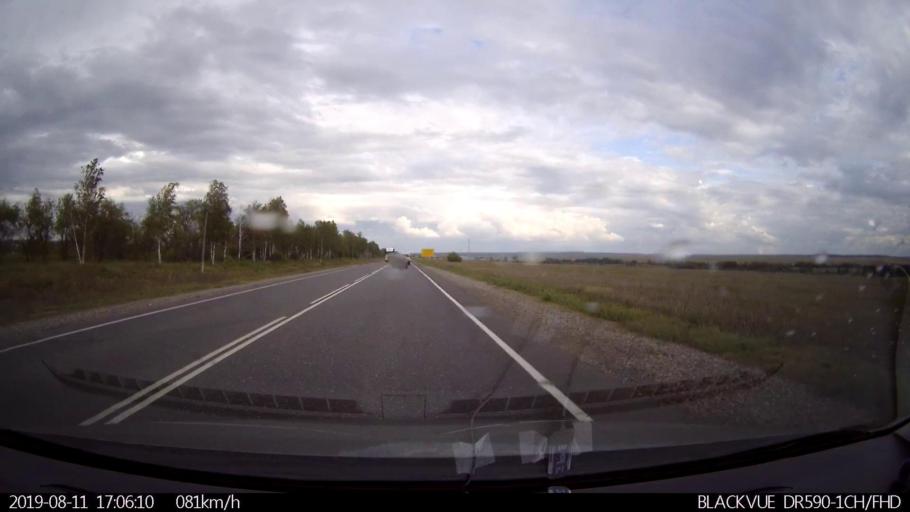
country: RU
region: Ulyanovsk
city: Mayna
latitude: 54.2954
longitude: 47.8008
